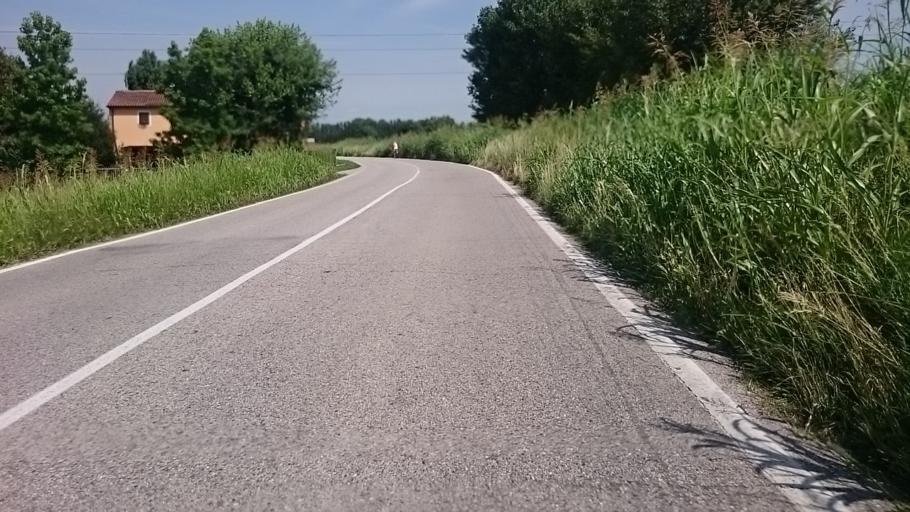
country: IT
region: Veneto
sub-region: Provincia di Vicenza
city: Montegaldella
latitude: 45.4321
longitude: 11.6771
